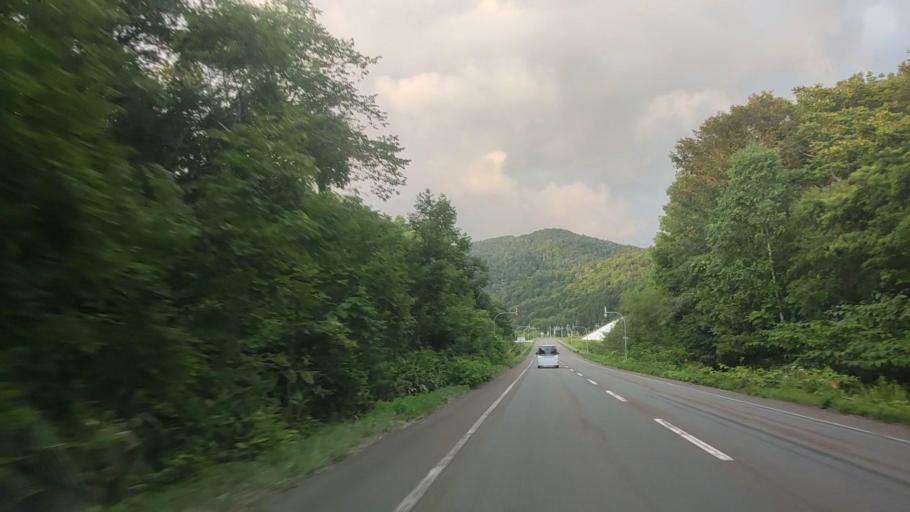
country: JP
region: Hokkaido
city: Ashibetsu
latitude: 43.3764
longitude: 142.2095
